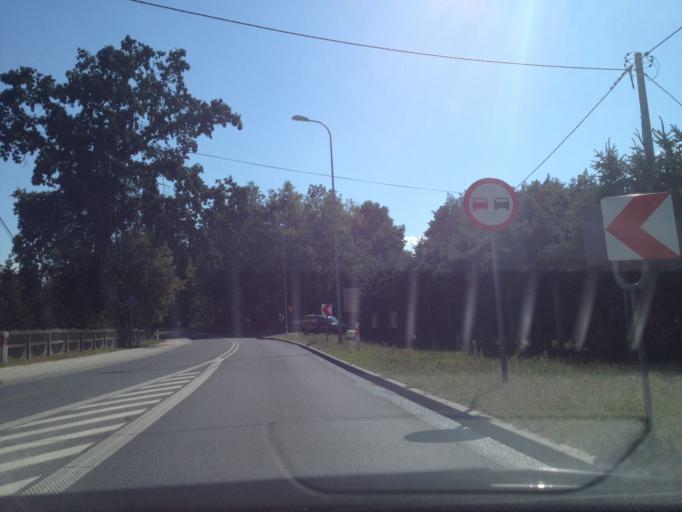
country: PL
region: Lubusz
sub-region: Powiat zaganski
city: Ilowa
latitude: 51.5204
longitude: 15.2143
